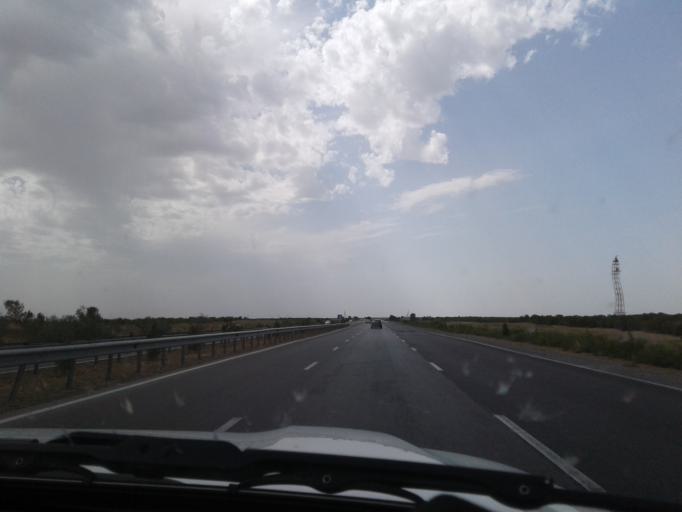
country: TM
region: Ahal
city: Annau
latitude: 37.8667
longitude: 58.6658
